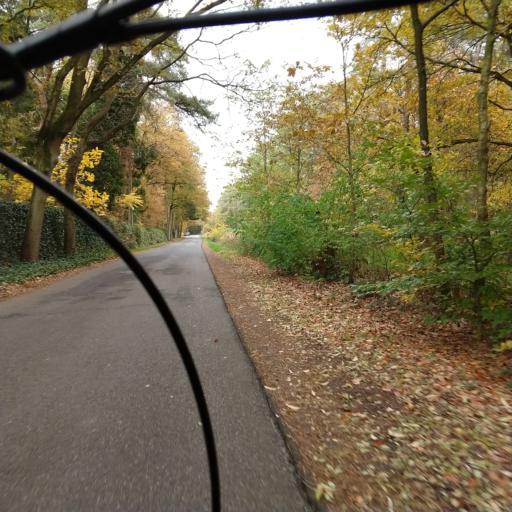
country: BE
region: Flanders
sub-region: Provincie Antwerpen
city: Kalmthout
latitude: 51.3988
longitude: 4.4544
